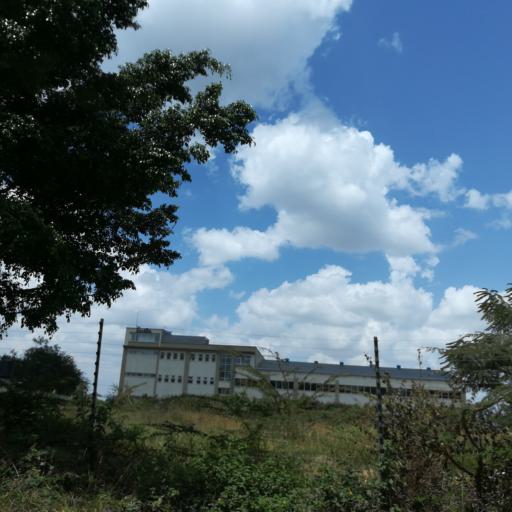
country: KE
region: Nairobi Area
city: Nairobi
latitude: -1.3223
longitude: 36.8080
